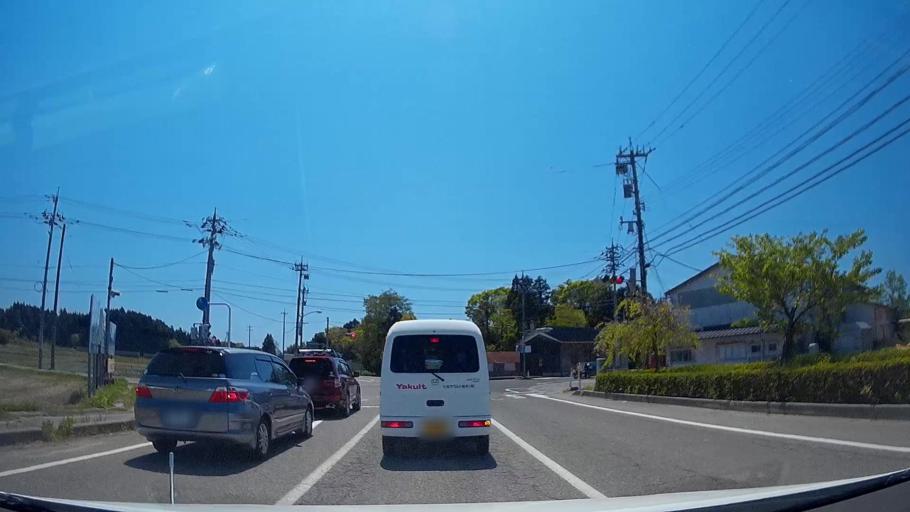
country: JP
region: Ishikawa
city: Nanao
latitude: 37.4505
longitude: 137.2971
